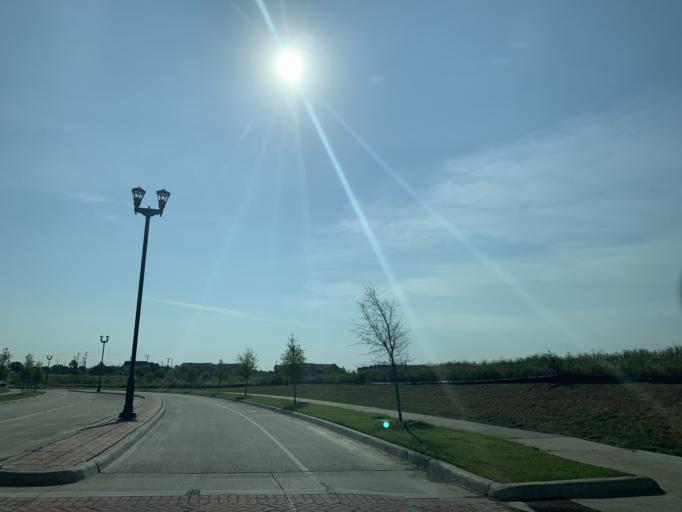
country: US
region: Texas
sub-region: Tarrant County
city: Blue Mound
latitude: 32.8894
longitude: -97.3111
